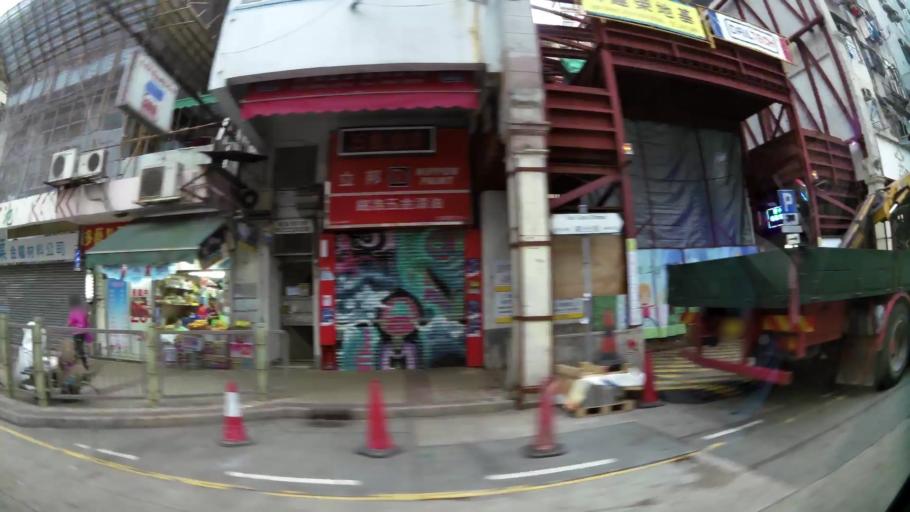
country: HK
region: Sham Shui Po
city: Sham Shui Po
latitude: 22.3217
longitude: 114.1638
